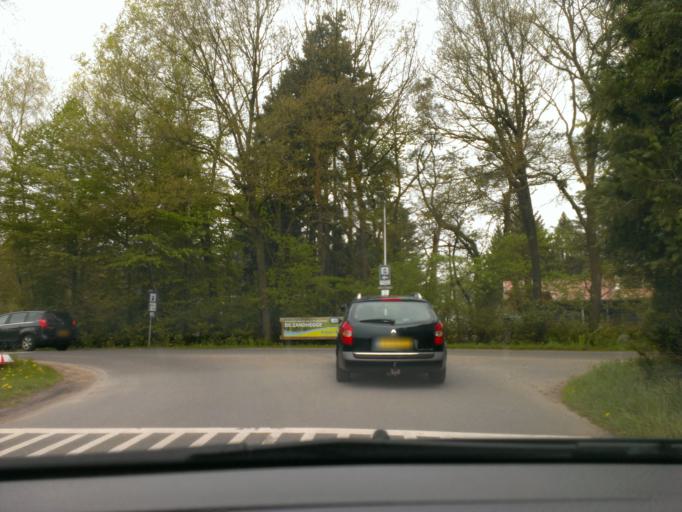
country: NL
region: Gelderland
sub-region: Gemeente Epe
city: Emst
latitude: 52.3303
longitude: 5.9630
